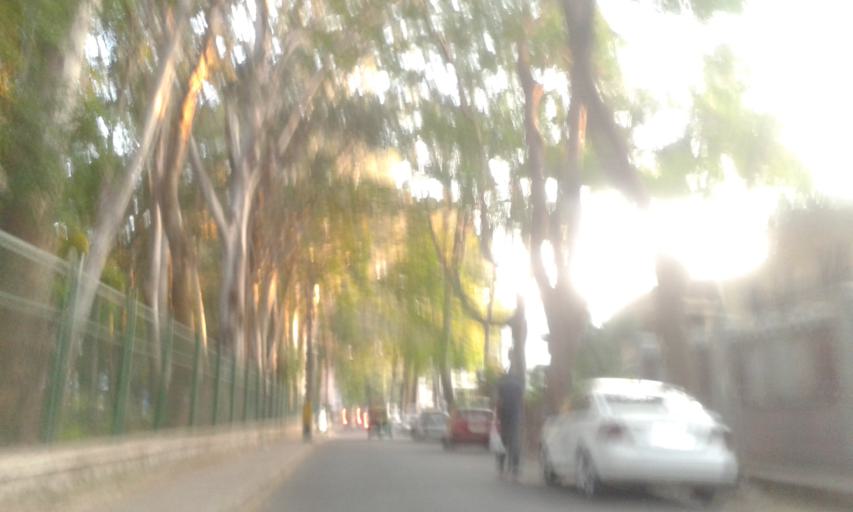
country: IN
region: Karnataka
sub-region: Bangalore Urban
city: Bangalore
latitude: 12.9122
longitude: 77.5987
